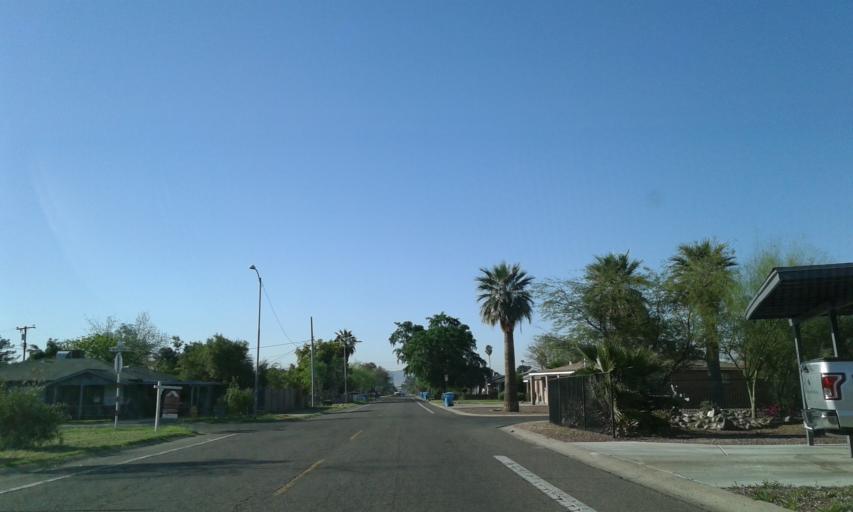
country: US
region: Arizona
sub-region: Maricopa County
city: Phoenix
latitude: 33.4900
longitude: -112.1084
